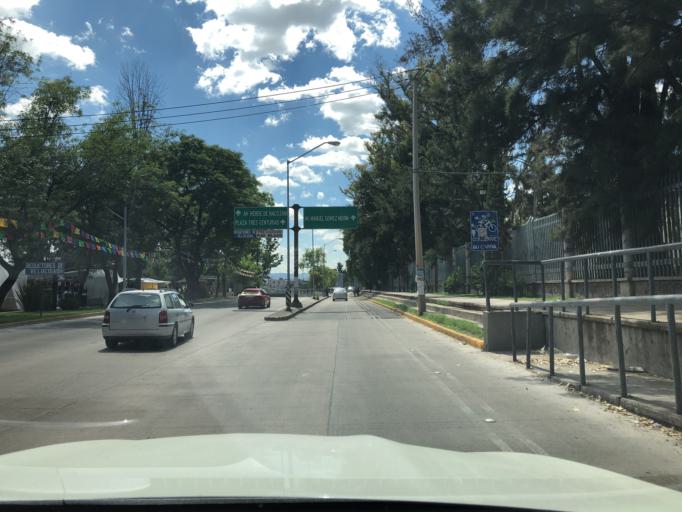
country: MX
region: Aguascalientes
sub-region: Aguascalientes
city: Aguascalientes
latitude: 21.8837
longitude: -102.2765
